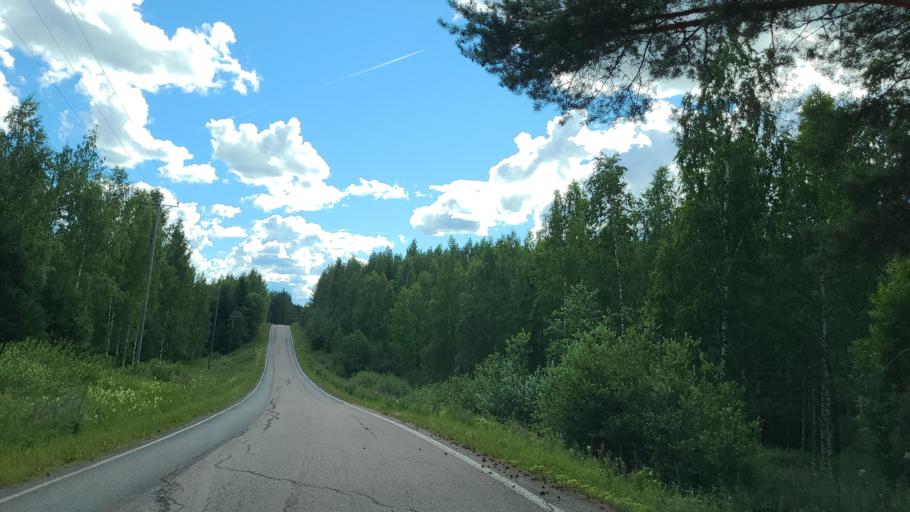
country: FI
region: Central Finland
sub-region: Jaemsae
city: Jaemsae
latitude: 61.8969
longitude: 25.2647
